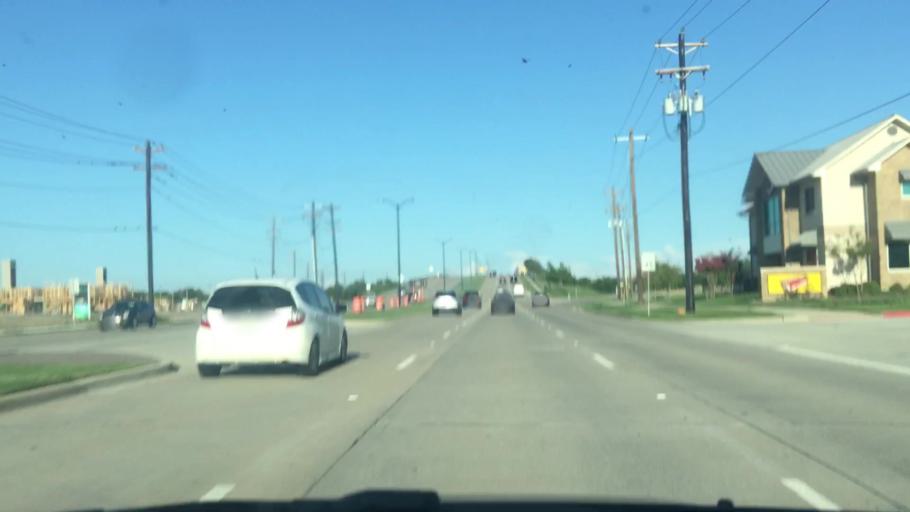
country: US
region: Texas
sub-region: Collin County
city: Frisco
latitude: 33.1747
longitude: -96.8277
